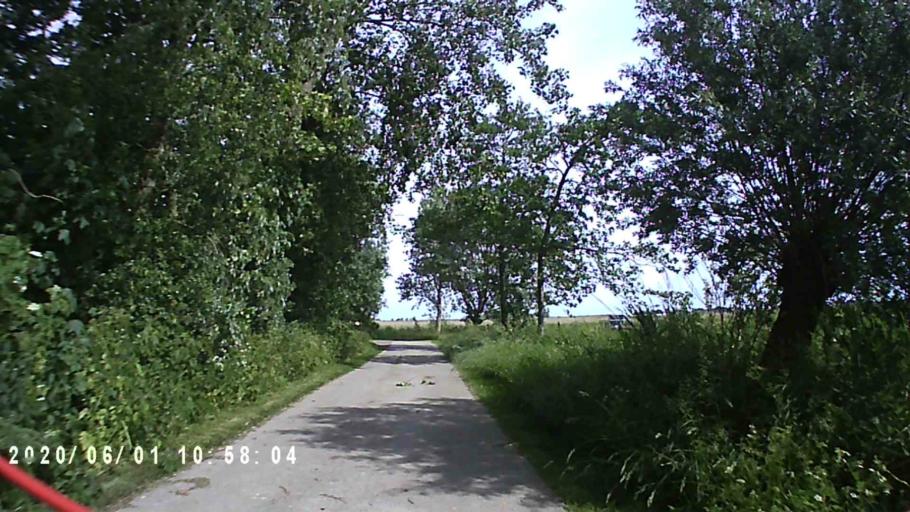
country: NL
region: Friesland
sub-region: Gemeente Franekeradeel
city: Sexbierum
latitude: 53.2007
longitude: 5.4926
